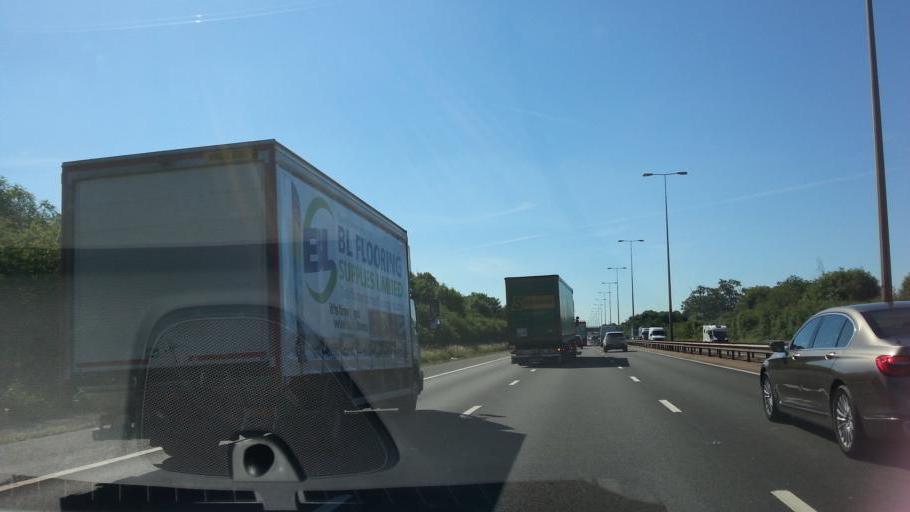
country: GB
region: England
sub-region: Worcestershire
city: Upton upon Severn
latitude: 52.0805
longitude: -2.1716
